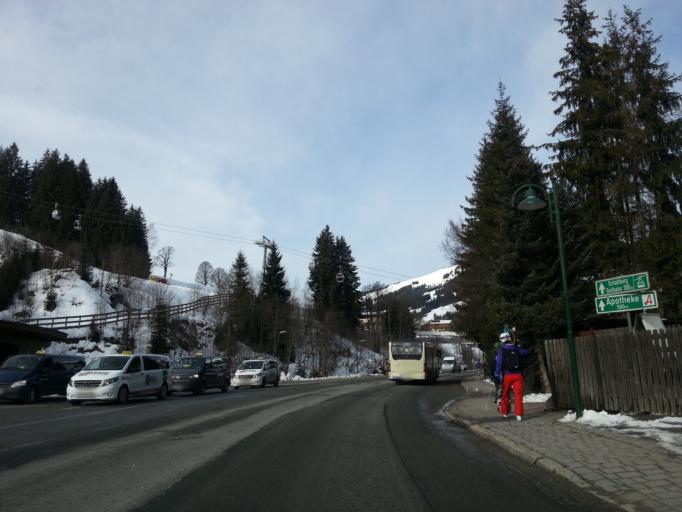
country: AT
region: Salzburg
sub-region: Politischer Bezirk Zell am See
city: Saalbach
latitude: 47.3894
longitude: 12.6370
